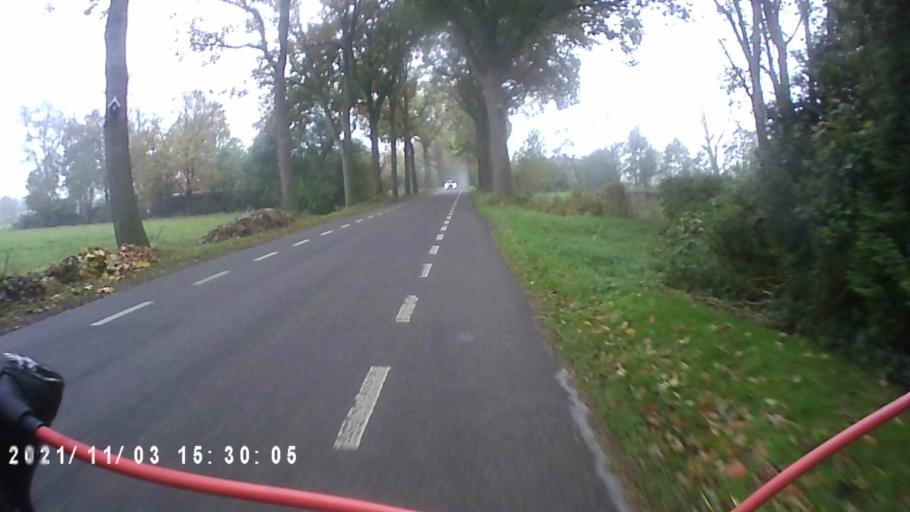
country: NL
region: Groningen
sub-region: Gemeente Leek
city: Leek
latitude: 53.1339
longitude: 6.3716
